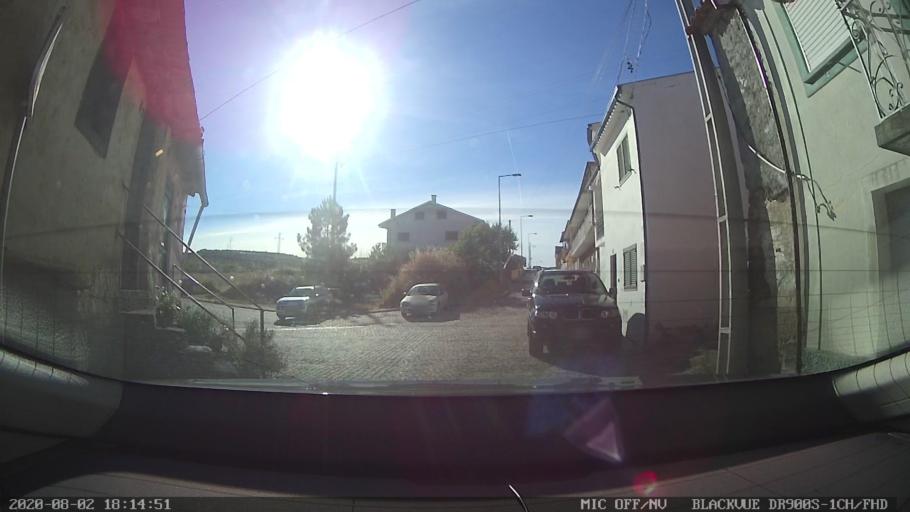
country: PT
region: Vila Real
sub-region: Murca
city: Murca
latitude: 41.4085
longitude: -7.4551
